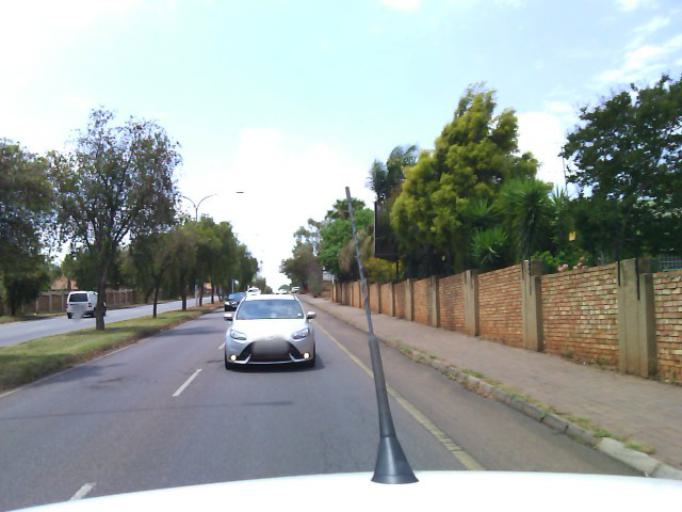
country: ZA
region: Gauteng
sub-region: City of Tshwane Metropolitan Municipality
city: Centurion
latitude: -25.8392
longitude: 28.1895
